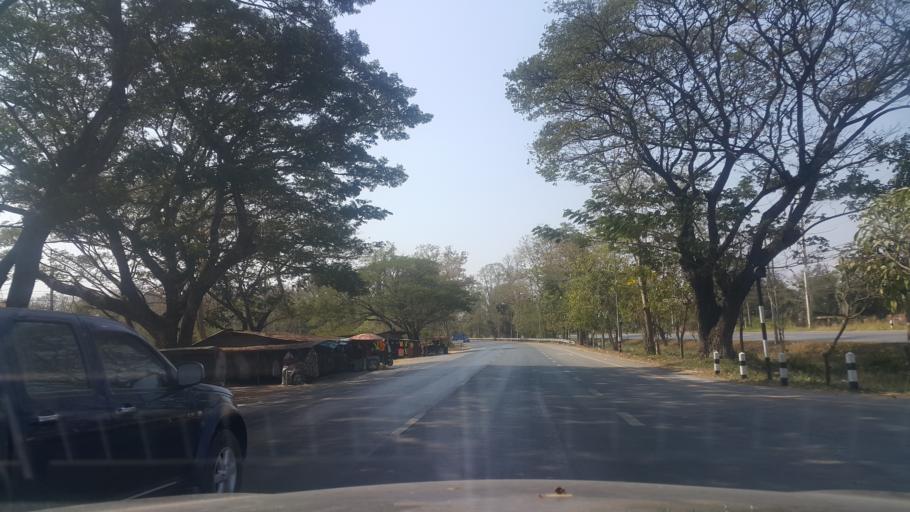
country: TH
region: Nakhon Ratchasima
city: Pak Thong Chai
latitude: 14.5683
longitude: 101.9801
